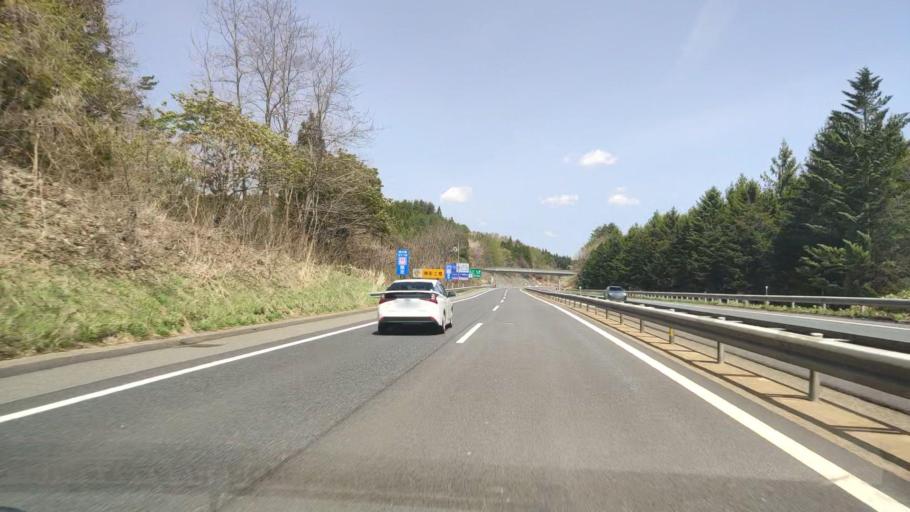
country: JP
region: Iwate
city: Ichinohe
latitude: 40.2435
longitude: 141.4010
